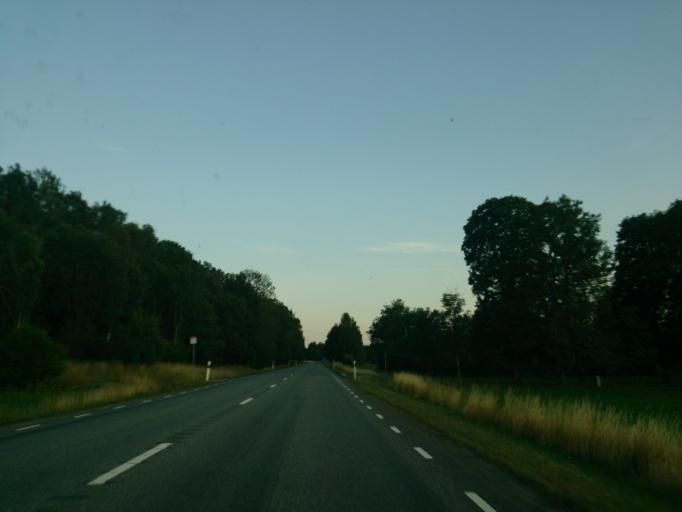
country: SE
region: Joenkoeping
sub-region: Varnamo Kommun
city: Bor
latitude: 57.0850
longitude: 14.1739
